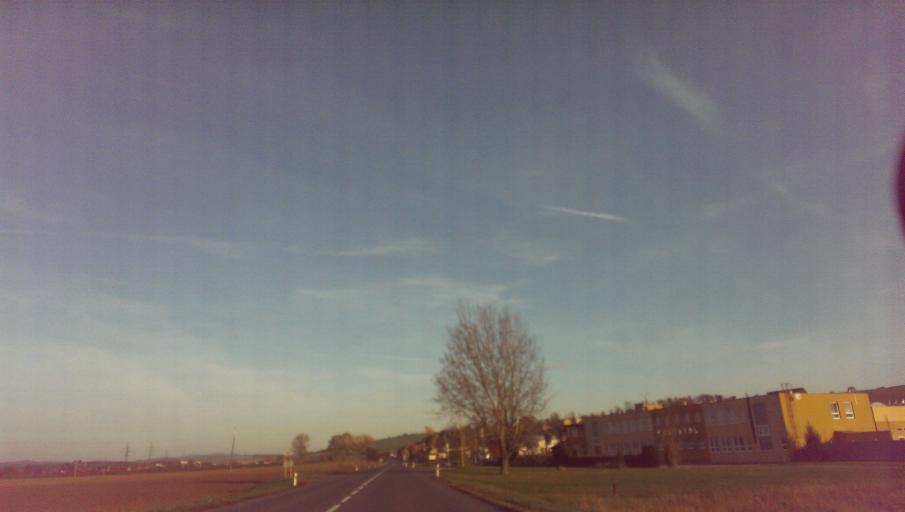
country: CZ
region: Zlin
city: Knezpole
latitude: 49.0903
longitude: 17.5052
